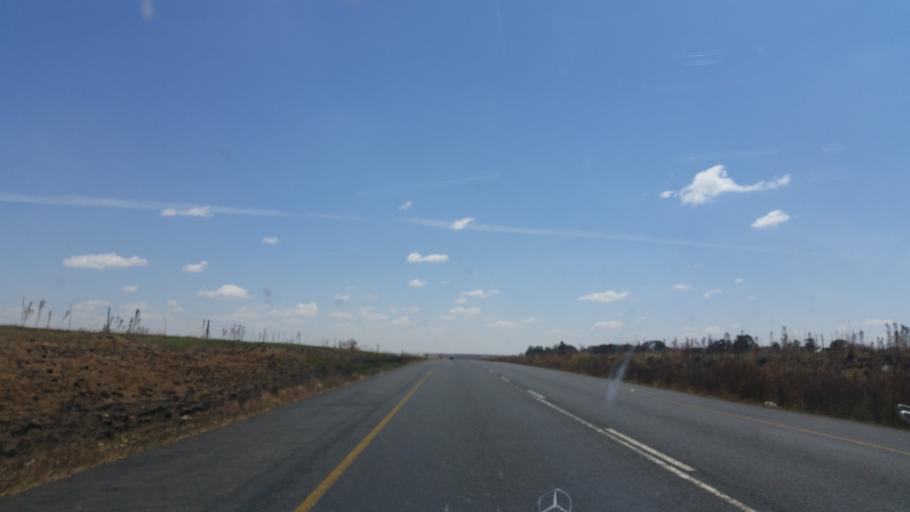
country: ZA
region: Orange Free State
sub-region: Thabo Mofutsanyana District Municipality
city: Bethlehem
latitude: -28.1091
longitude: 28.6675
